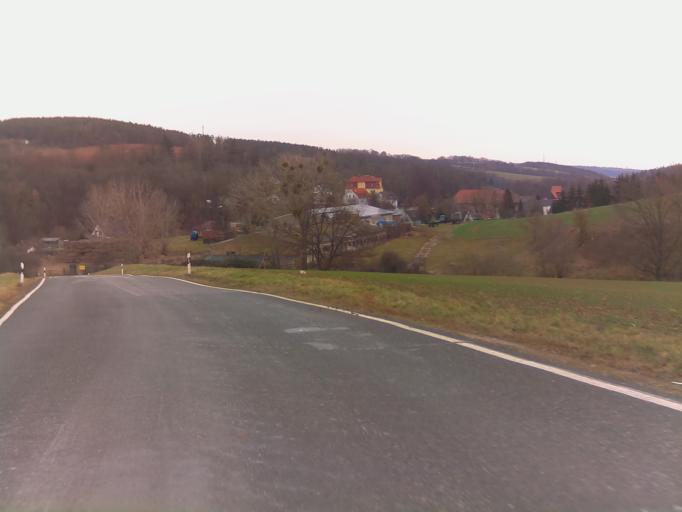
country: DE
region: Thuringia
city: Saara
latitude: 50.8789
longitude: 11.9667
